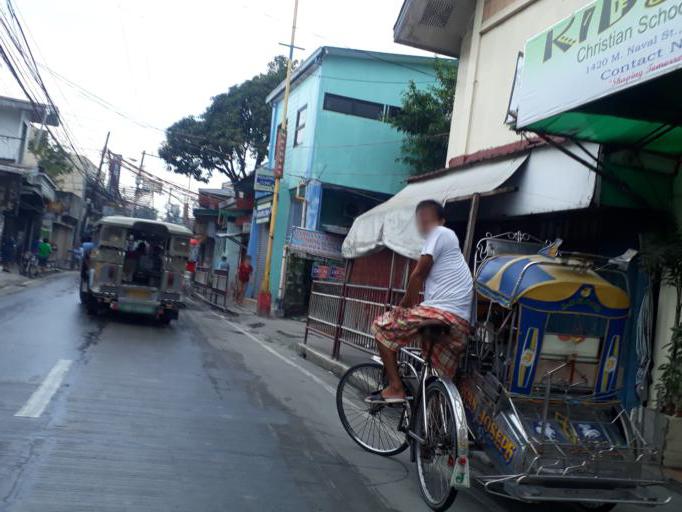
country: PH
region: Calabarzon
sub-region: Province of Rizal
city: Malabon
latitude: 14.6718
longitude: 120.9377
